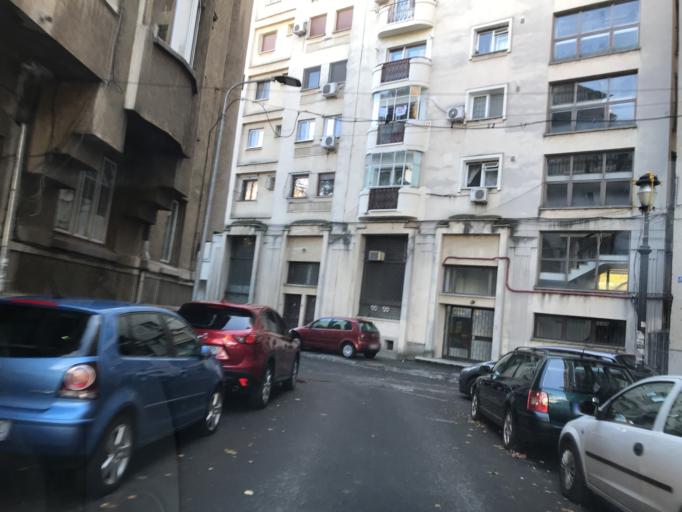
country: RO
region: Bucuresti
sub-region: Municipiul Bucuresti
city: Bucuresti
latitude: 44.4279
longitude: 26.0940
